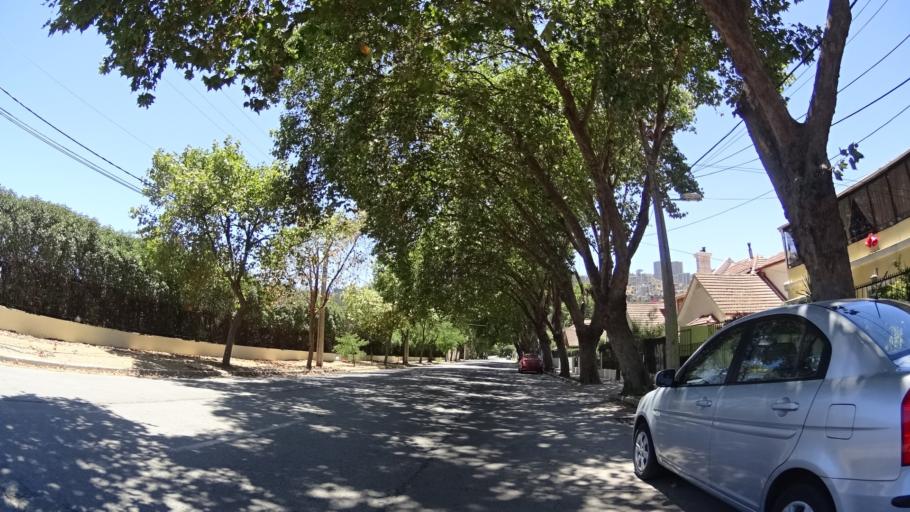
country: CL
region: Valparaiso
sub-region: Provincia de Valparaiso
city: Vina del Mar
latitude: -33.0275
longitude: -71.5344
